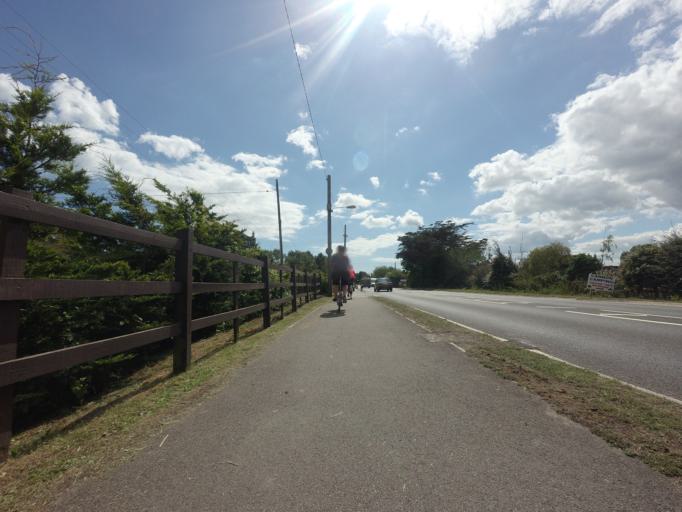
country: GB
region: England
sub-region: East Sussex
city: Pevensey
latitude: 50.8057
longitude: 0.3380
